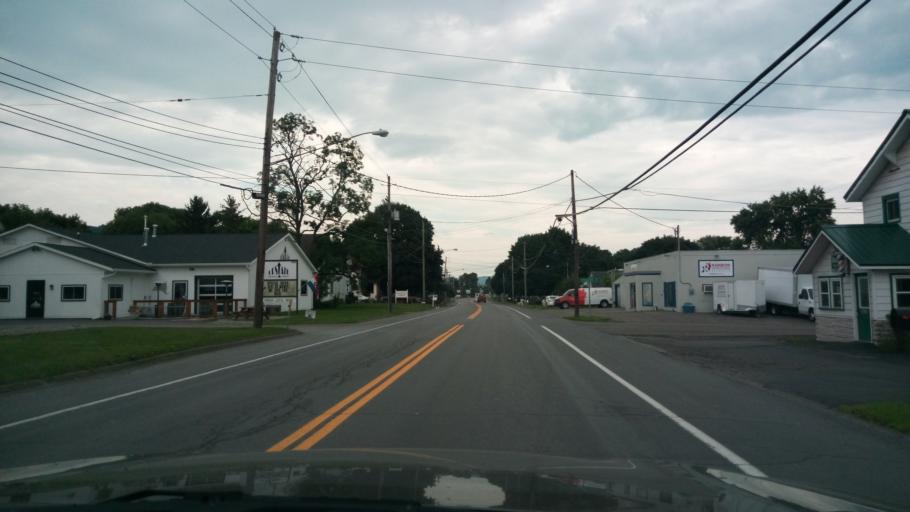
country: US
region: New York
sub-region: Chemung County
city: Elmira Heights
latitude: 42.1336
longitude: -76.8123
